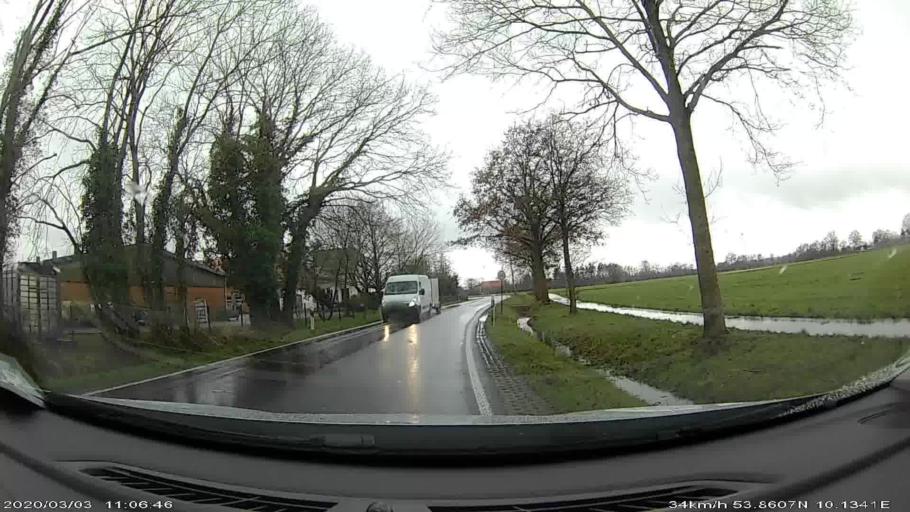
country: DE
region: Schleswig-Holstein
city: Stuvenborn
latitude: 53.8586
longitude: 10.1334
